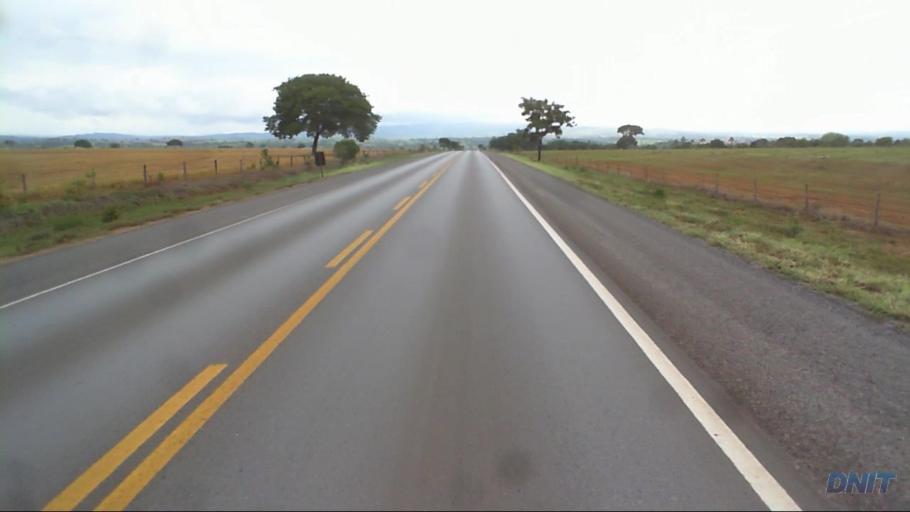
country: BR
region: Goias
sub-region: Padre Bernardo
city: Padre Bernardo
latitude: -15.2169
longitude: -48.6086
